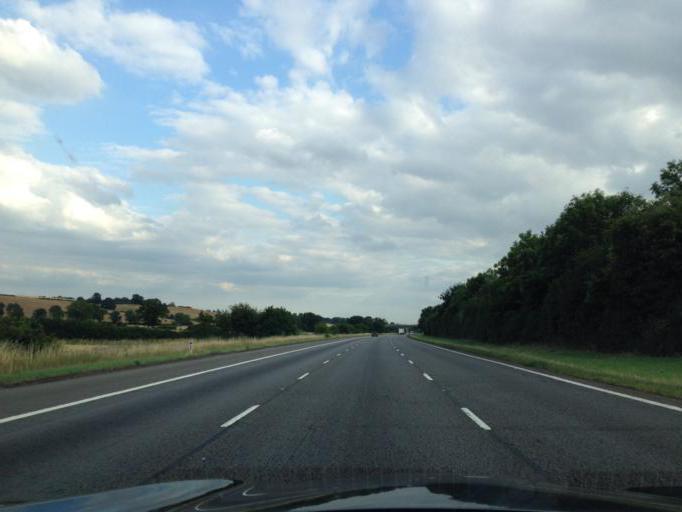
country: GB
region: England
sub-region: Oxfordshire
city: Hanwell
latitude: 52.1125
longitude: -1.3657
